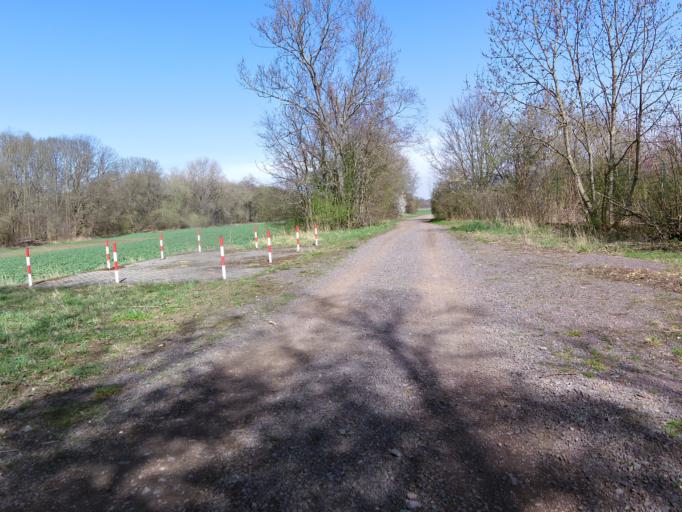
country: DE
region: Saxony
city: Schkeuditz
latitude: 51.3729
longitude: 12.2742
